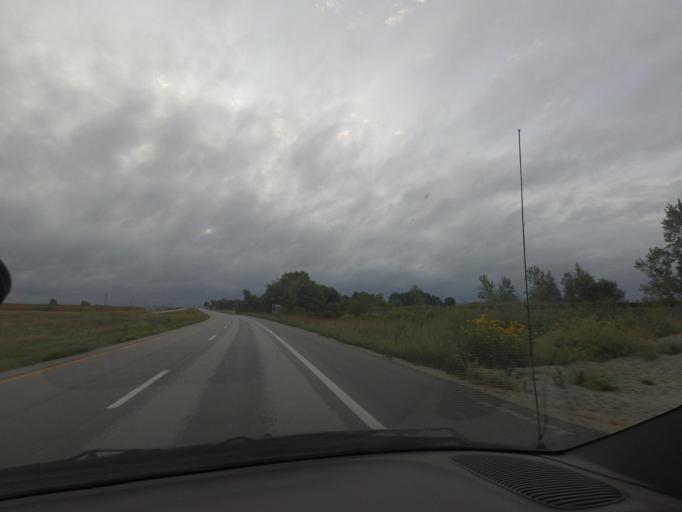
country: US
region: Missouri
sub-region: Shelby County
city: Shelbina
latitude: 39.6747
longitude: -91.9590
